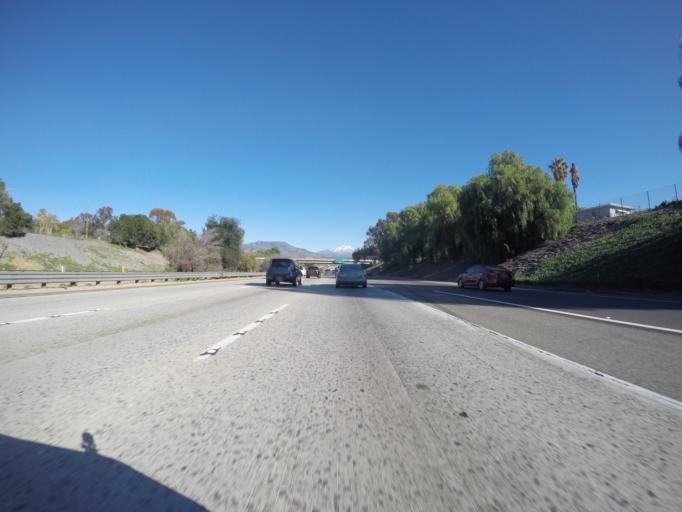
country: US
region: California
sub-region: San Bernardino County
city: San Bernardino
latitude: 34.1448
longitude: -117.2752
